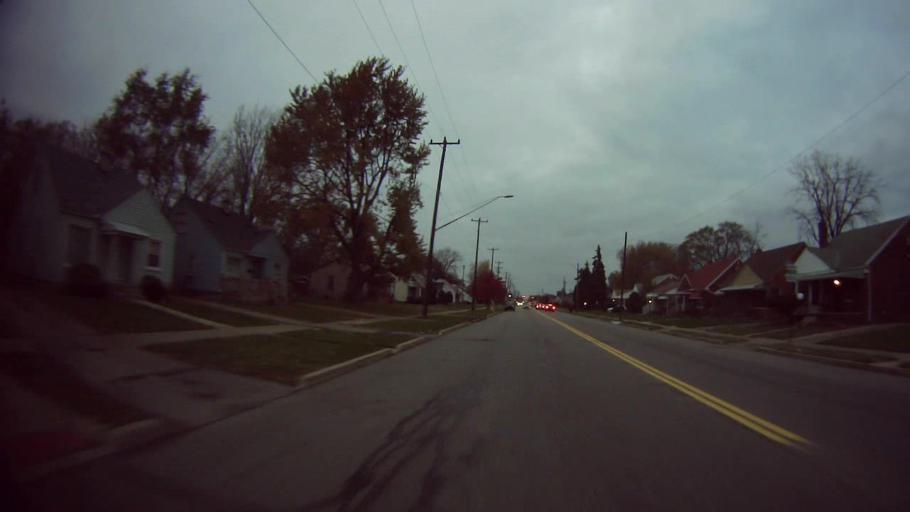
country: US
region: Michigan
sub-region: Oakland County
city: Hazel Park
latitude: 42.4440
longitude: -83.0638
